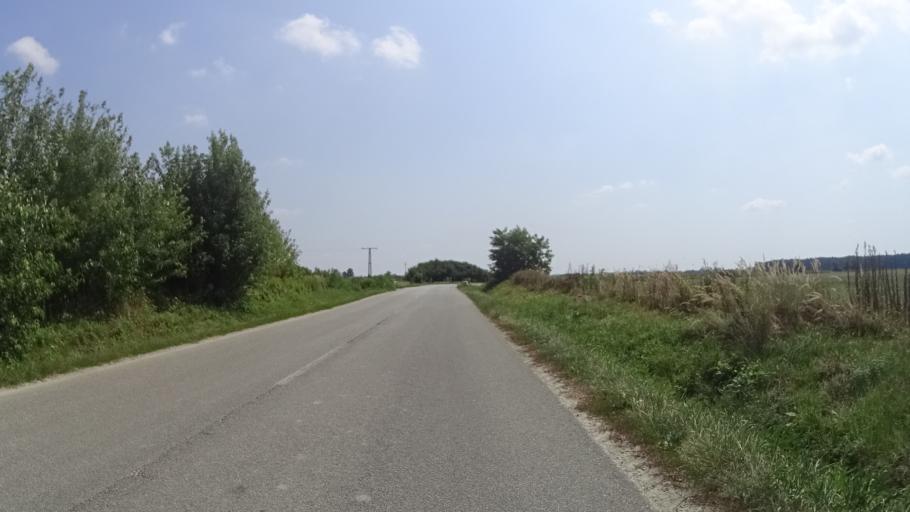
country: HU
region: Zala
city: Becsehely
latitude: 46.4157
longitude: 16.7754
